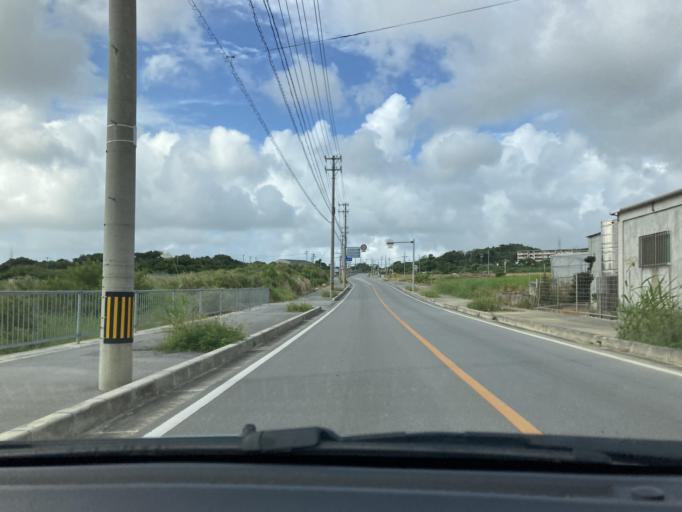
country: JP
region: Okinawa
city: Itoman
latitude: 26.1156
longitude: 127.6919
